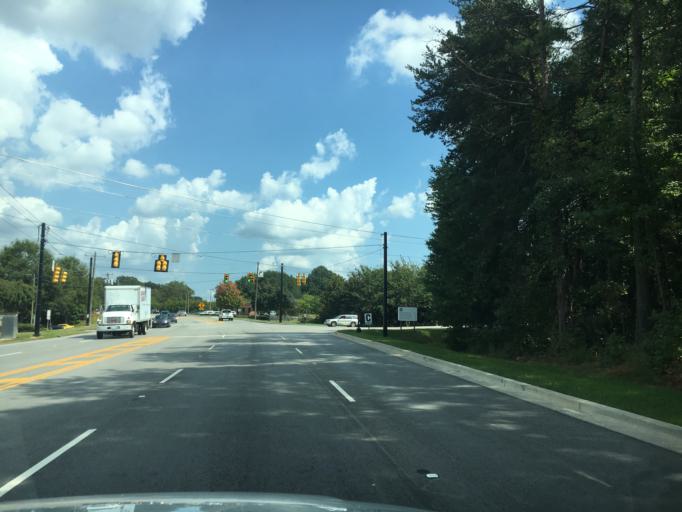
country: US
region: South Carolina
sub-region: Greenville County
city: Mauldin
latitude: 34.8355
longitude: -82.2841
